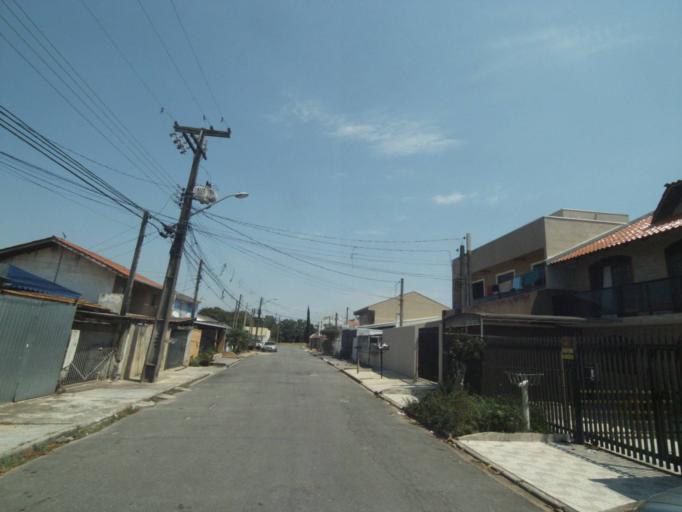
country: BR
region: Parana
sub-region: Sao Jose Dos Pinhais
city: Sao Jose dos Pinhais
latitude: -25.5205
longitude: -49.2673
